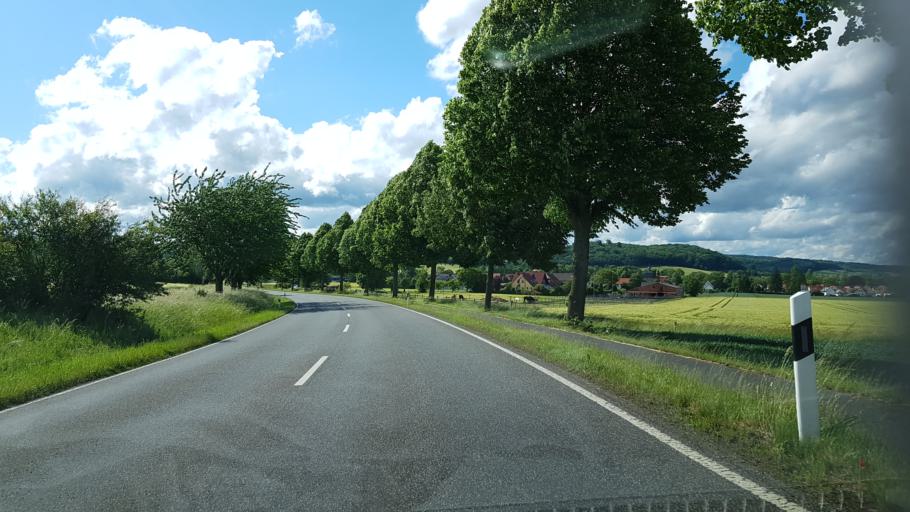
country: DE
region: Lower Saxony
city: Bovenden
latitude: 51.5942
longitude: 9.8664
